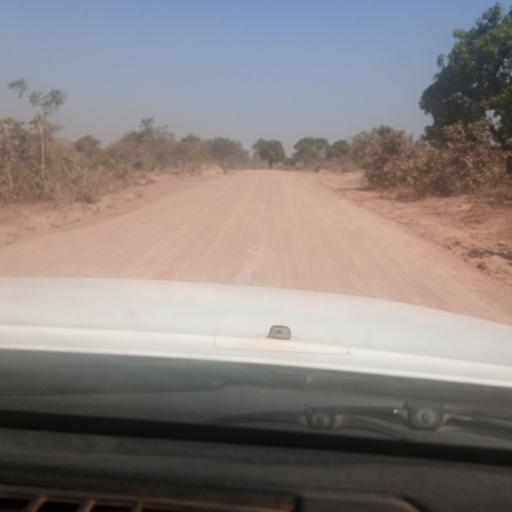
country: NG
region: Adamawa
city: Yola
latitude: 9.0962
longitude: 12.3899
